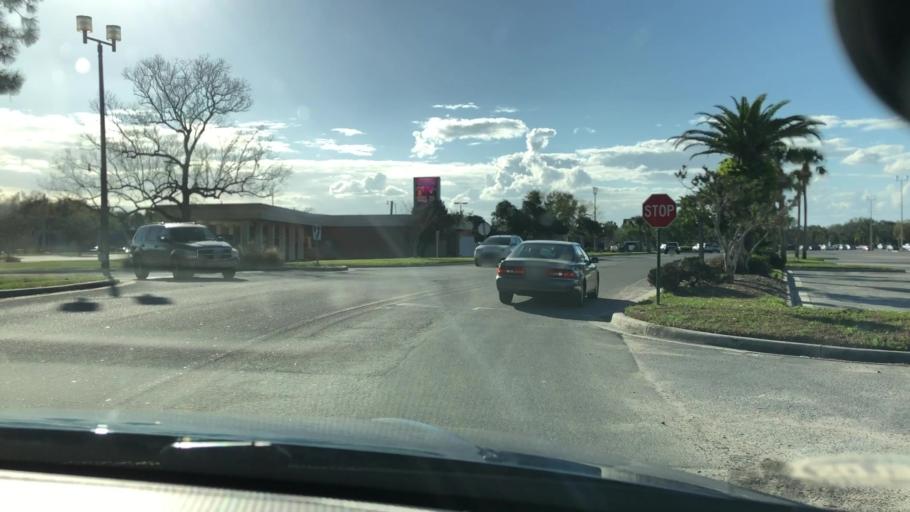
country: US
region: Florida
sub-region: Lake County
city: Silver Lake
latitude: 28.8230
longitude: -81.7831
